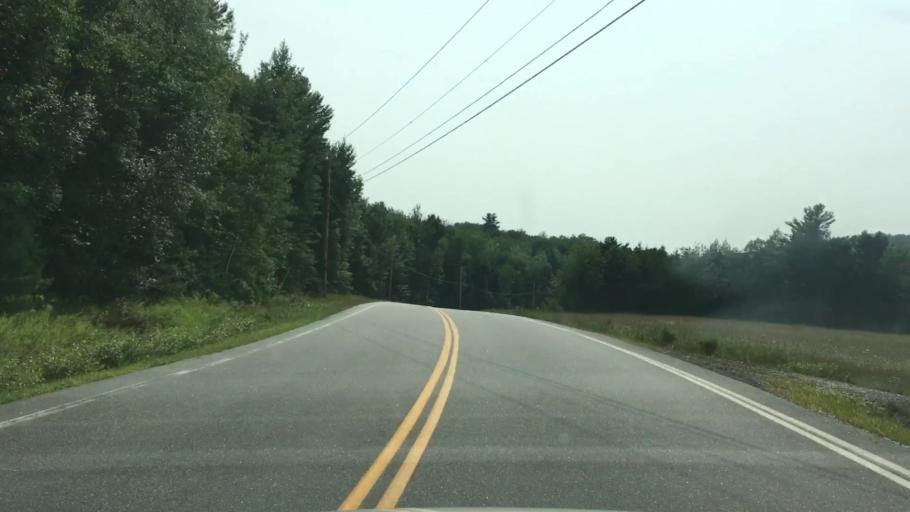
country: US
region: Maine
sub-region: Oxford County
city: Buckfield
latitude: 44.2662
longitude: -70.4236
